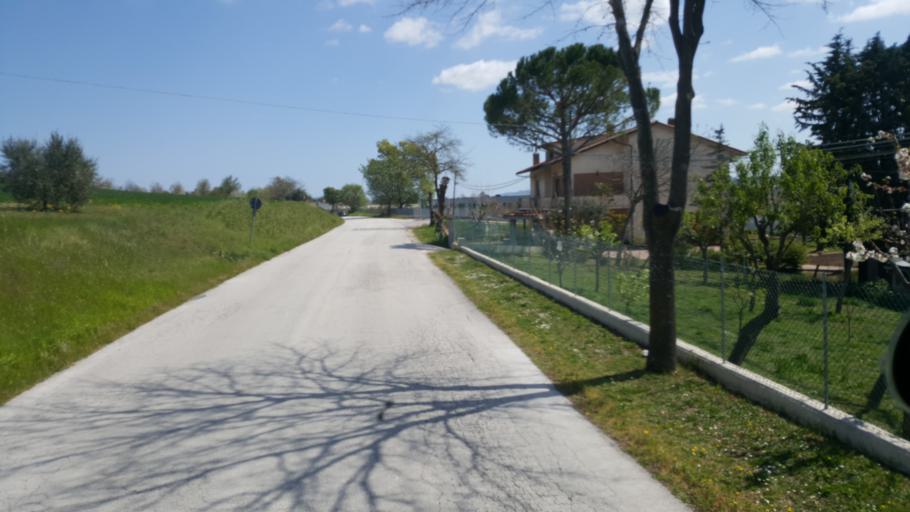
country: IT
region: The Marches
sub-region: Provincia di Macerata
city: Montecassiano
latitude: 43.3552
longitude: 13.4520
